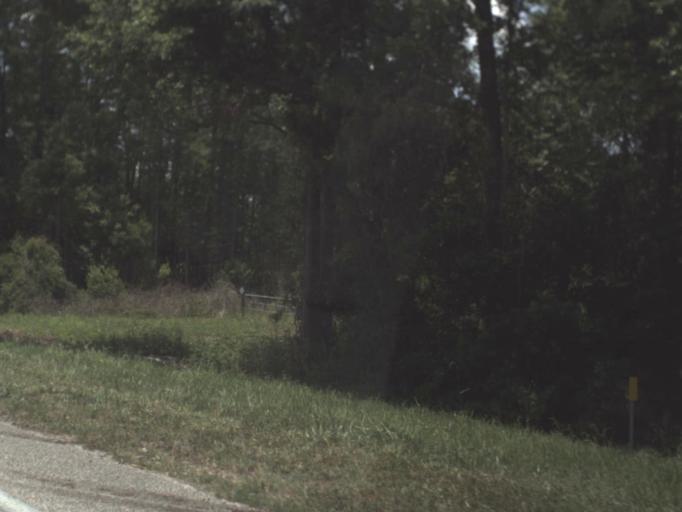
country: US
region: Florida
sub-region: Bradford County
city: Starke
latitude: 29.8792
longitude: -82.1504
